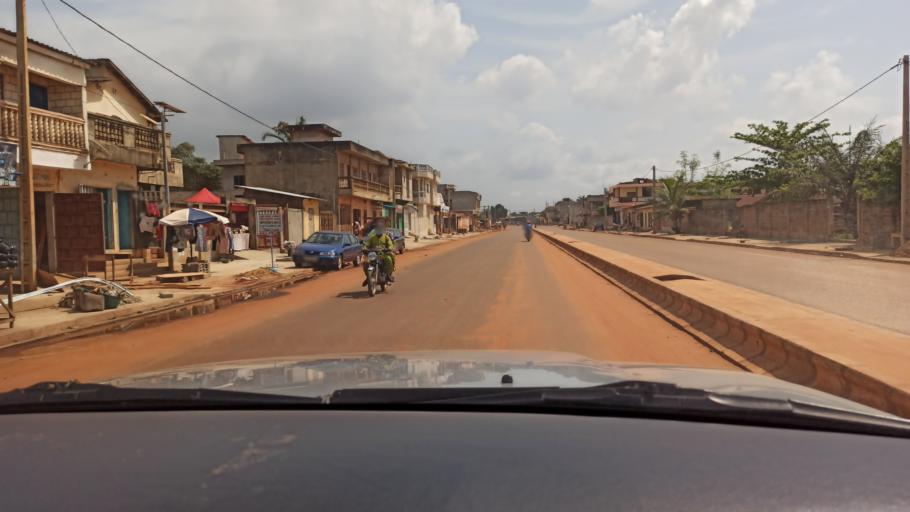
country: BJ
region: Queme
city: Porto-Novo
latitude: 6.4816
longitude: 2.5928
